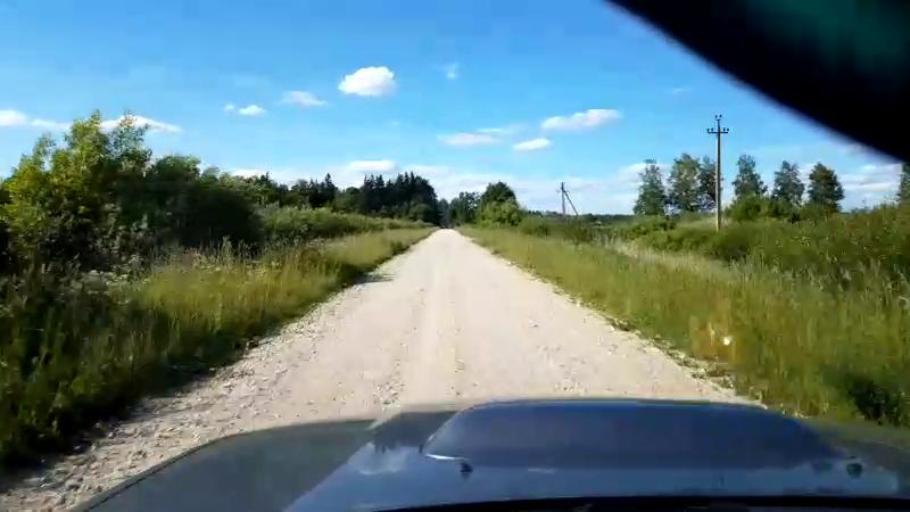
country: EE
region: Paernumaa
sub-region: Sauga vald
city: Sauga
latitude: 58.5075
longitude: 24.5641
